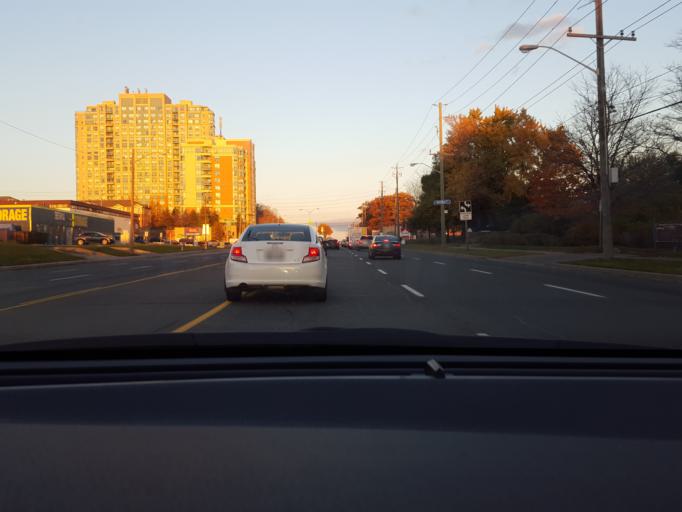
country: CA
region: Ontario
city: Scarborough
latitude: 43.7696
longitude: -79.2637
